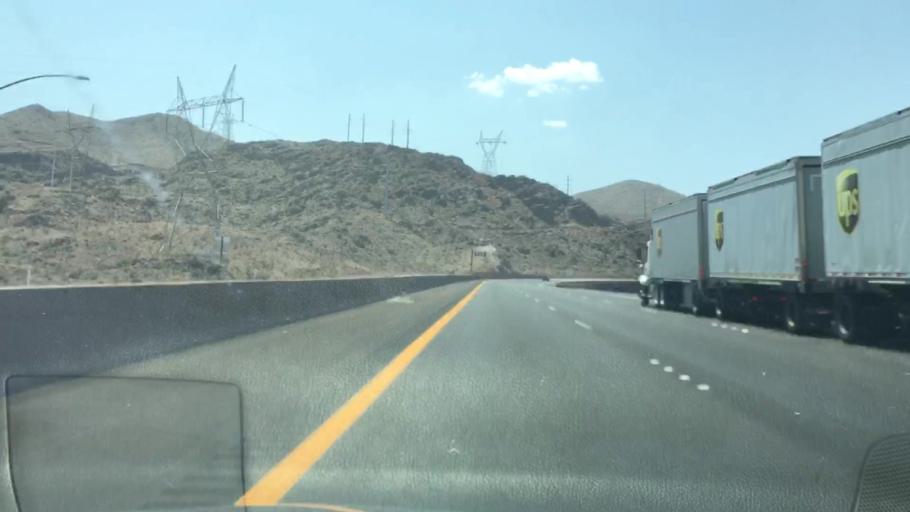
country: US
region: Nevada
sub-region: Clark County
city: Boulder City
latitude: 36.0076
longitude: -114.7805
